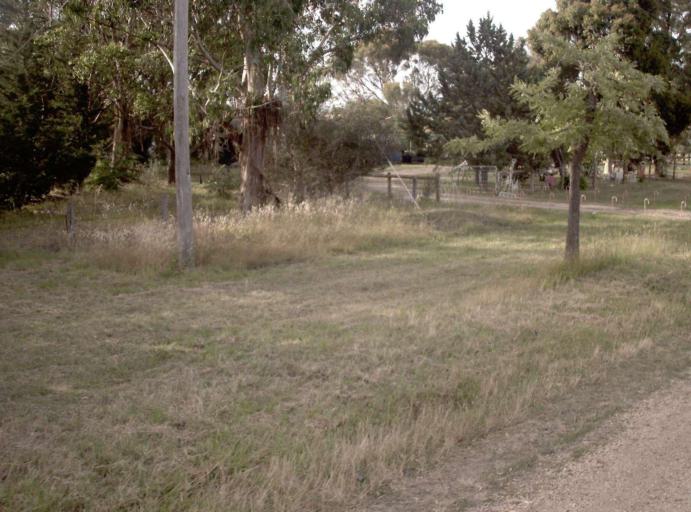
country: AU
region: Victoria
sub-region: Wellington
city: Sale
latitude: -37.9450
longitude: 146.9891
